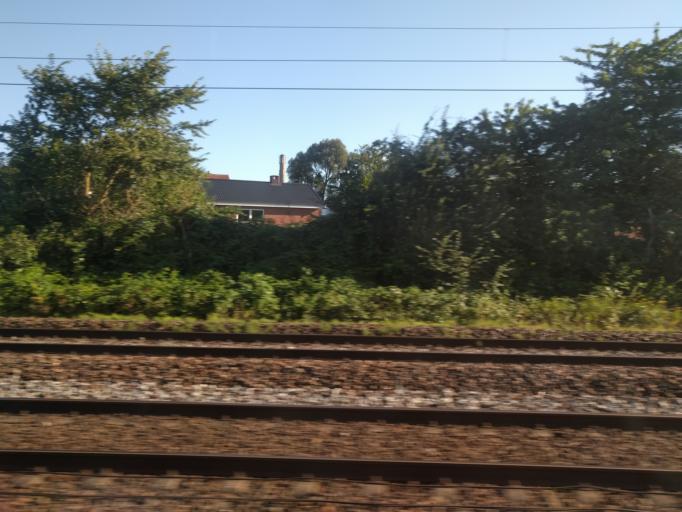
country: DK
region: Capital Region
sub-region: Hoje-Taastrup Kommune
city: Flong
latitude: 55.6482
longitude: 12.2001
